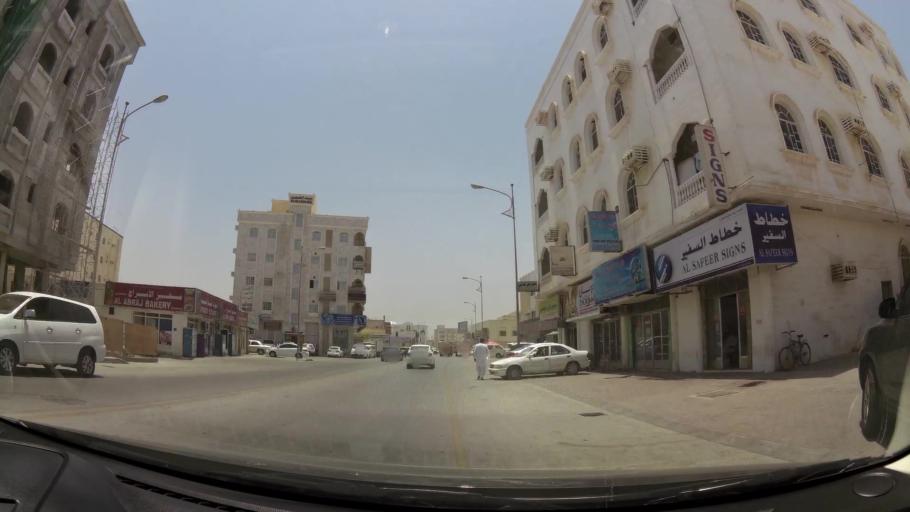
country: OM
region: Zufar
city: Salalah
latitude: 17.0162
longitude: 54.1064
